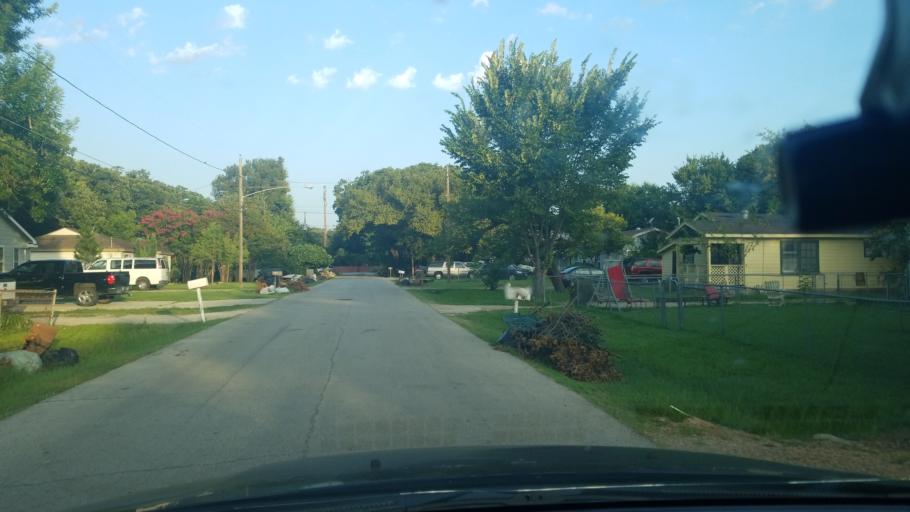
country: US
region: Texas
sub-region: Dallas County
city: Balch Springs
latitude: 32.7290
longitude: -96.6551
